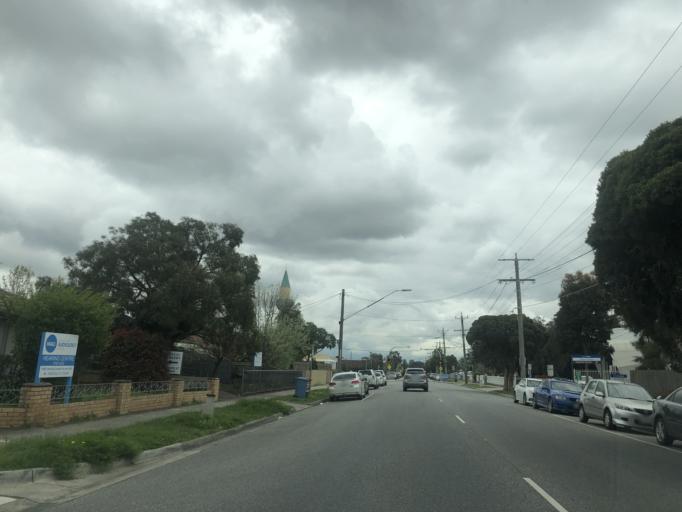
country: AU
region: Victoria
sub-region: Greater Dandenong
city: Dandenong North
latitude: -37.9758
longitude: 145.2163
